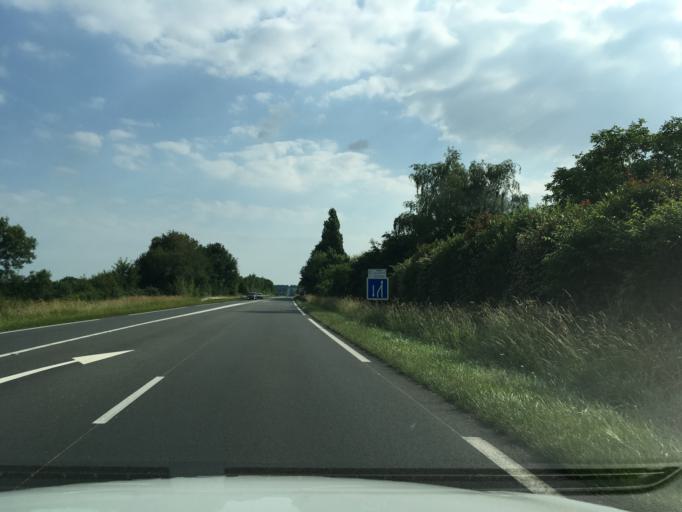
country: FR
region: Poitou-Charentes
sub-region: Departement des Deux-Sevres
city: Saint-Pardoux
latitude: 46.5749
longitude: -0.2947
